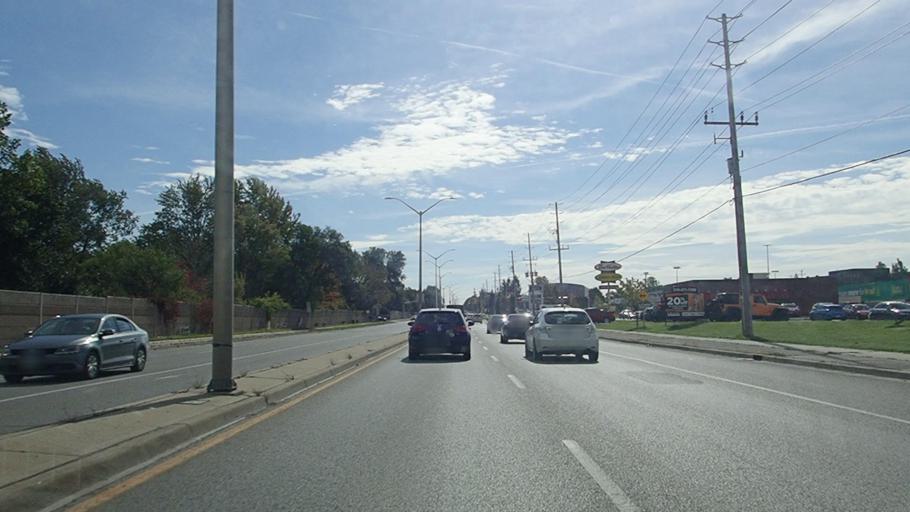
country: CA
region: Ontario
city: London
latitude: 43.0063
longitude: -81.3041
